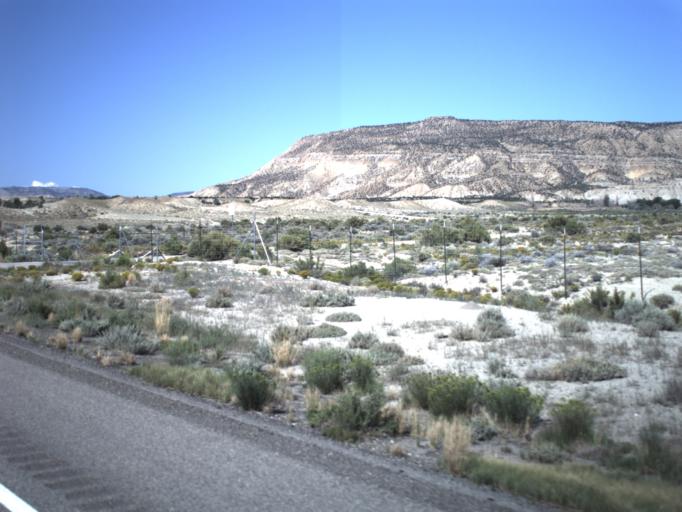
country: US
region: Utah
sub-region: Emery County
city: Ferron
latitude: 38.9398
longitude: -111.2227
